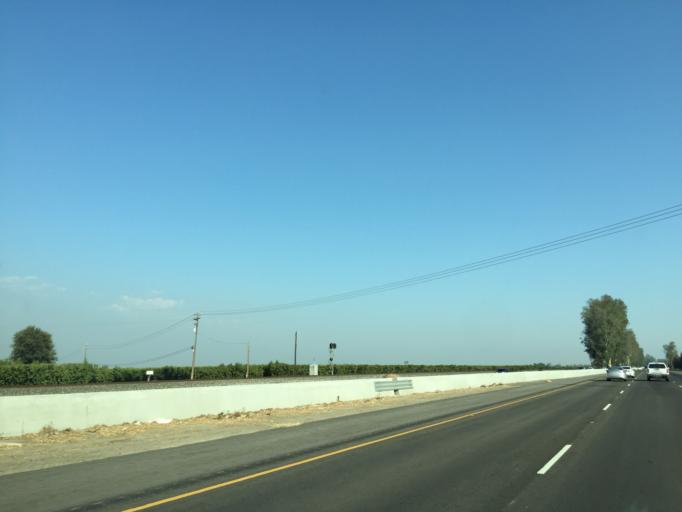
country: US
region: California
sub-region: Tulare County
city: London
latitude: 36.4744
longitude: -119.5028
